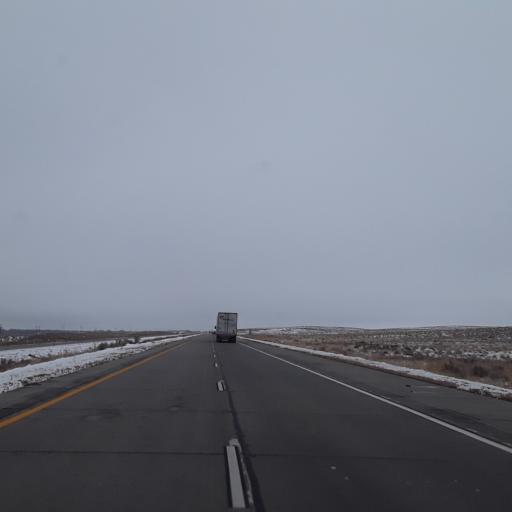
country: US
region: Colorado
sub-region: Logan County
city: Sterling
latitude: 40.5704
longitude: -103.2043
